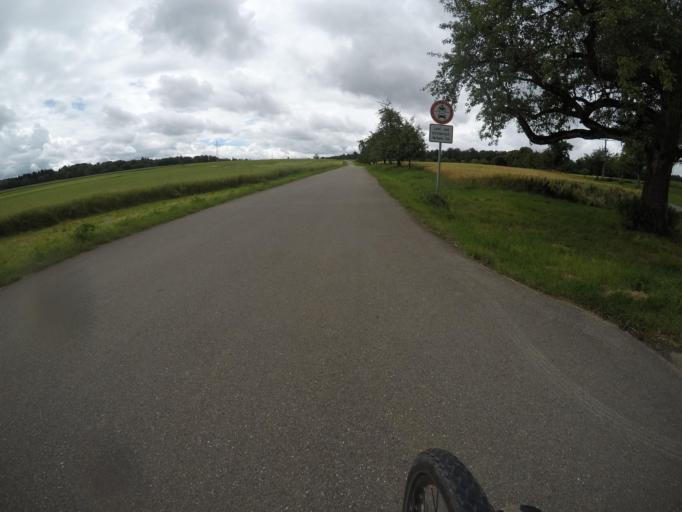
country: DE
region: Baden-Wuerttemberg
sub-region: Regierungsbezirk Stuttgart
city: Oberjettingen
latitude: 48.6048
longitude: 8.8121
